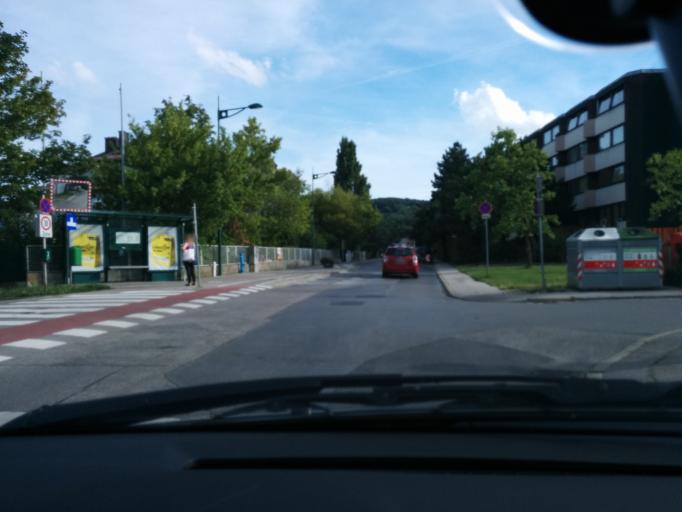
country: AT
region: Lower Austria
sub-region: Politischer Bezirk Modling
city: Modling
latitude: 48.0748
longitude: 16.2957
